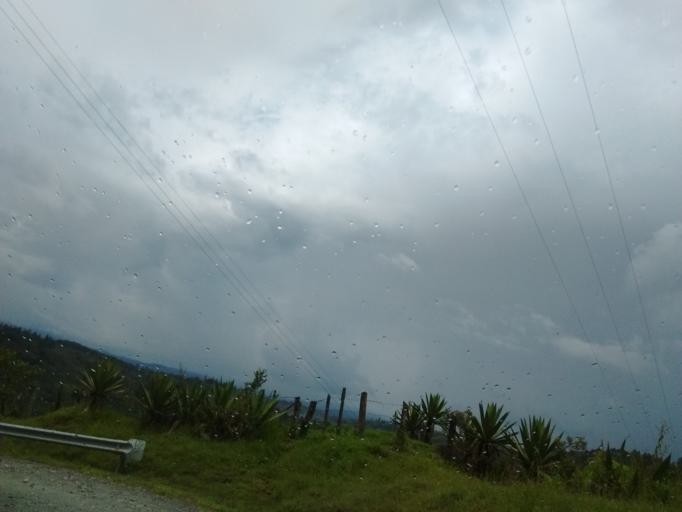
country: CO
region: Cauca
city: Cajibio
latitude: 2.5610
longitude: -76.6341
